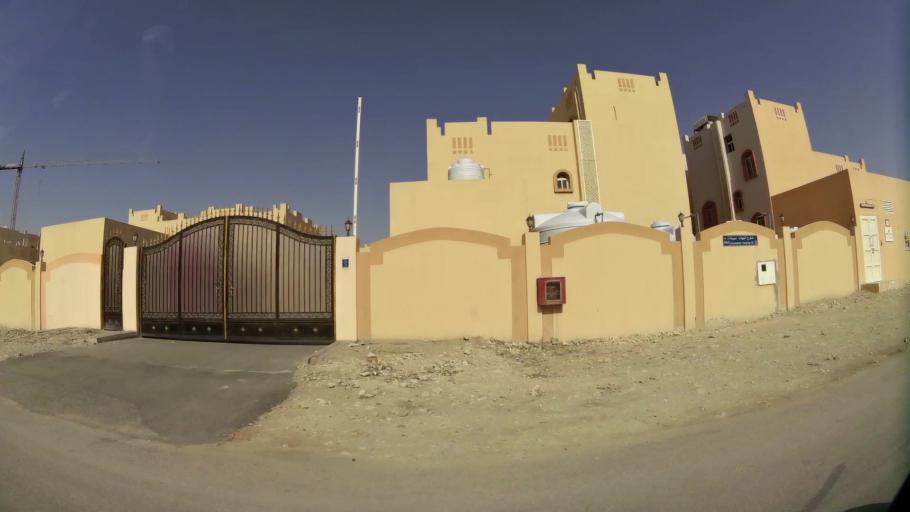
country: QA
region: Baladiyat ar Rayyan
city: Ar Rayyan
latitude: 25.3454
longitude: 51.4285
